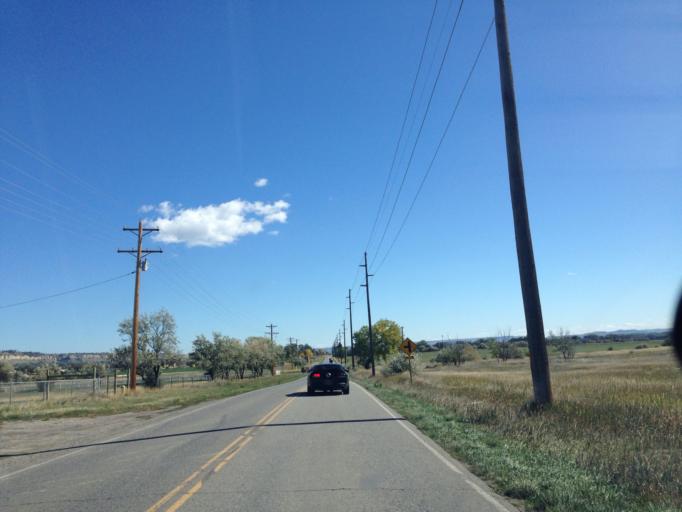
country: US
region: Montana
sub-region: Yellowstone County
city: Laurel
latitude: 45.7841
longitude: -108.6762
